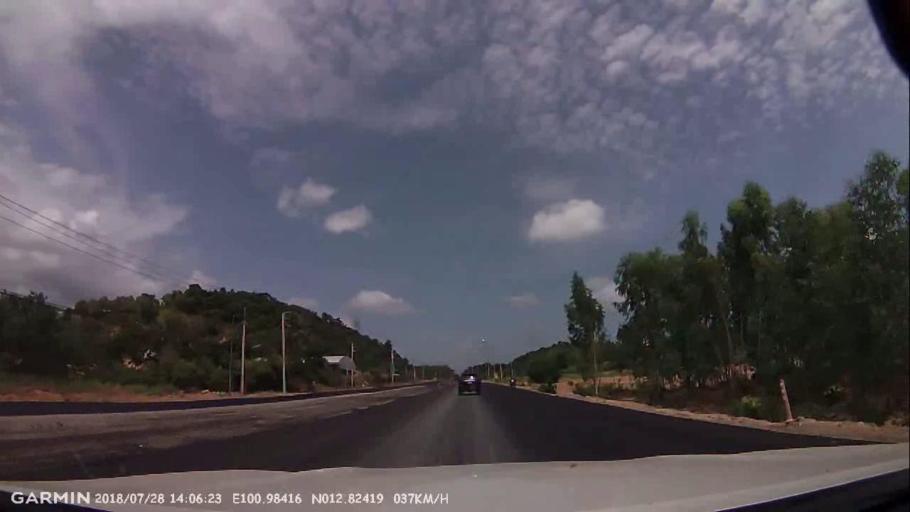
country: TH
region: Rayong
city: Ban Chang
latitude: 12.8241
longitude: 100.9843
